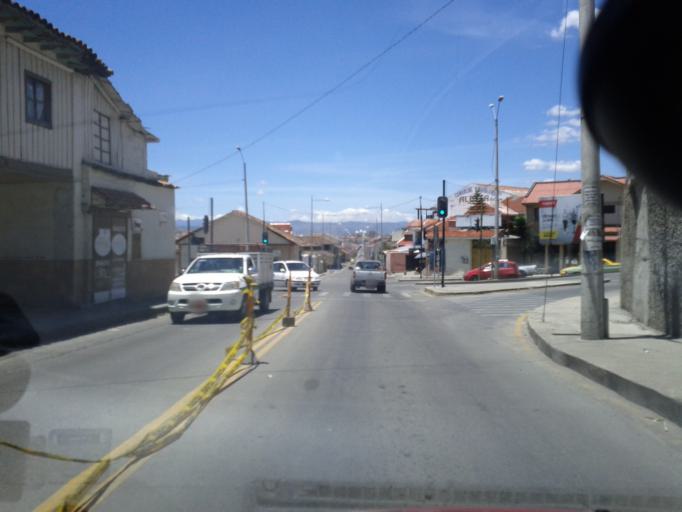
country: EC
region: Azuay
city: Cuenca
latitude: -2.9048
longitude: -79.0254
